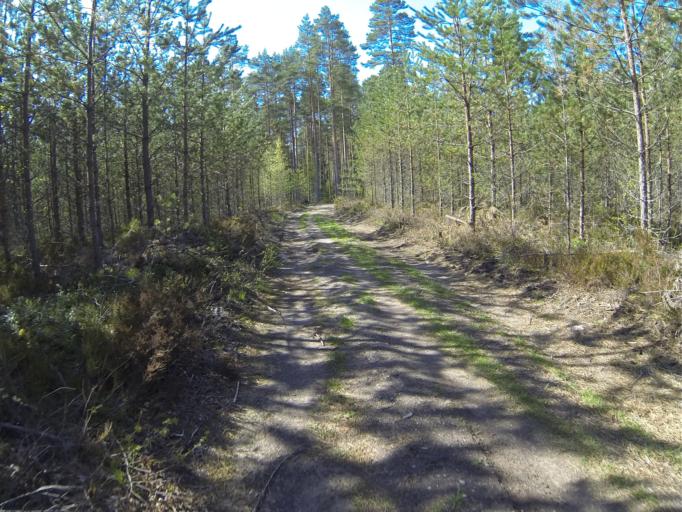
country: FI
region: Varsinais-Suomi
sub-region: Salo
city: Pertteli
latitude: 60.3915
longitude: 23.2153
